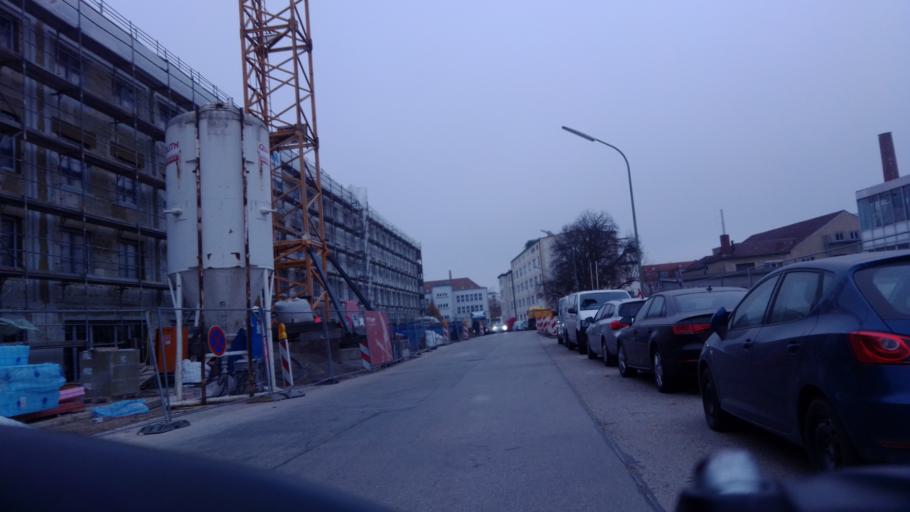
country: DE
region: Bavaria
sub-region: Upper Bavaria
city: Pullach im Isartal
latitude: 48.1019
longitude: 11.5382
